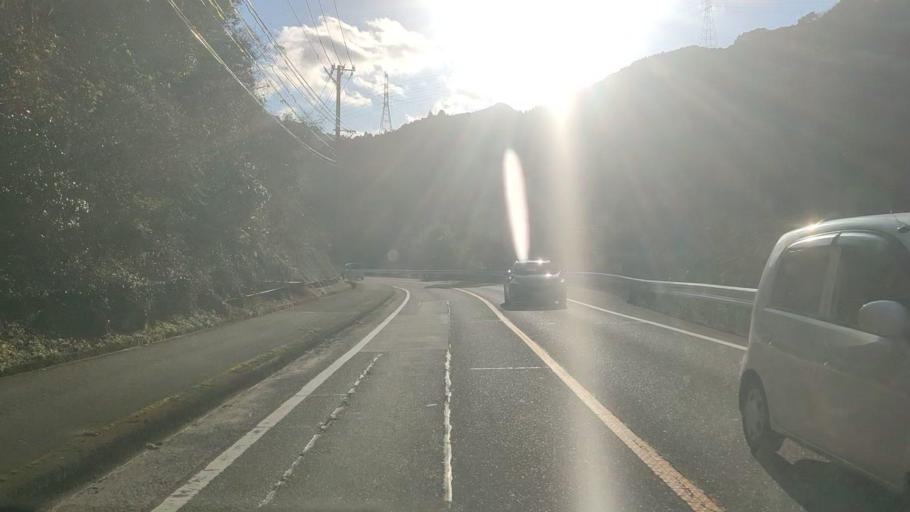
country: JP
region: Saga Prefecture
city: Saga-shi
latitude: 33.3469
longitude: 130.2487
